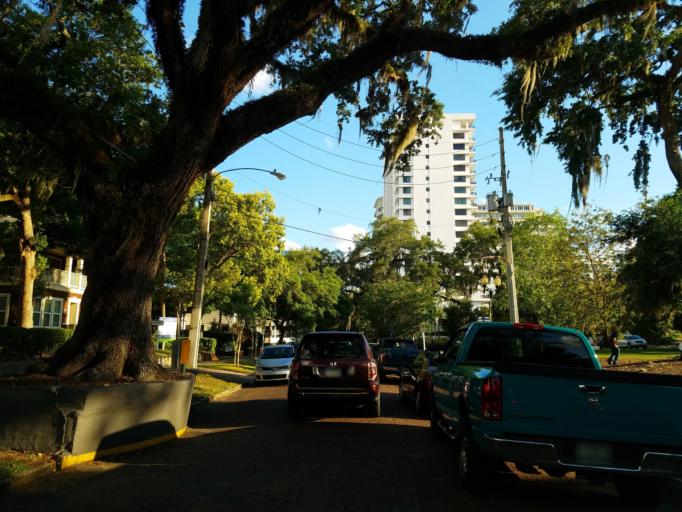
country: US
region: Florida
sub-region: Orange County
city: Orlando
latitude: 28.5432
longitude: -81.3699
